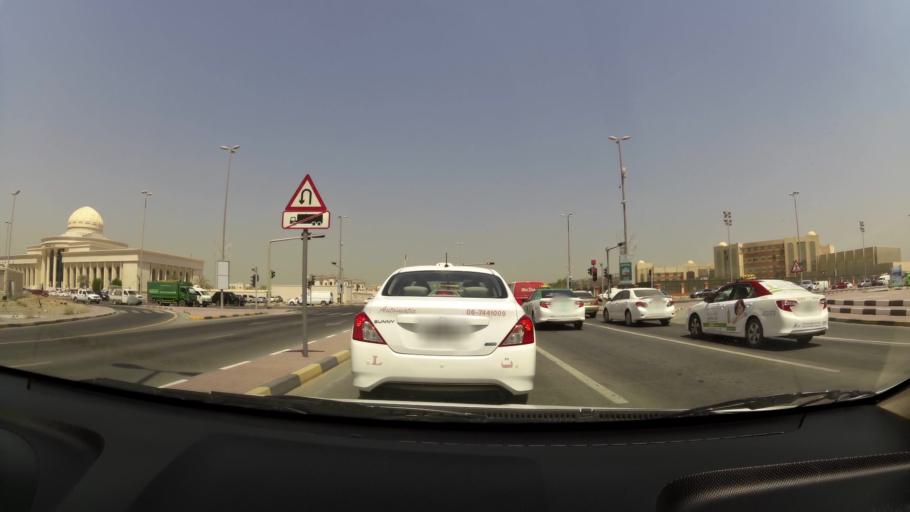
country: AE
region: Ajman
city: Ajman
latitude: 25.4093
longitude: 55.5094
